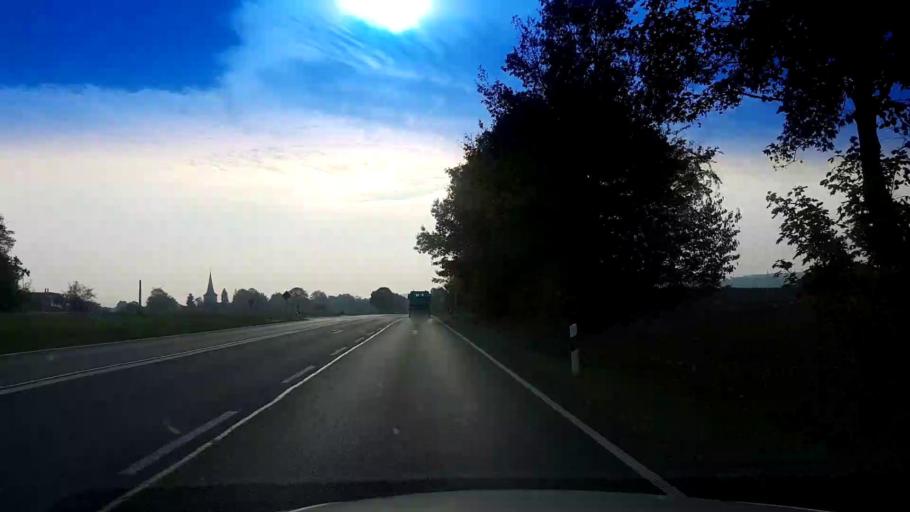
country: DE
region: Bavaria
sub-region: Upper Franconia
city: Mainleus
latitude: 50.1122
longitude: 11.3528
